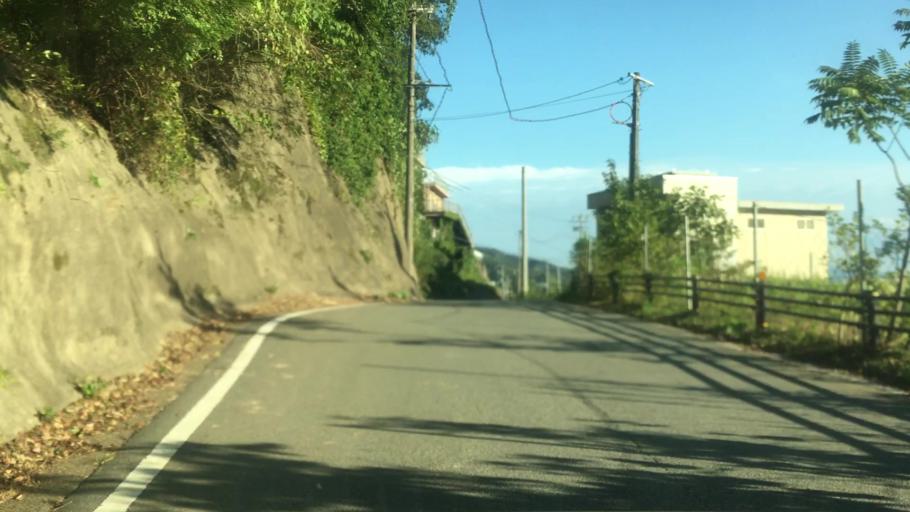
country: JP
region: Hyogo
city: Toyooka
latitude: 35.5878
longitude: 134.8043
